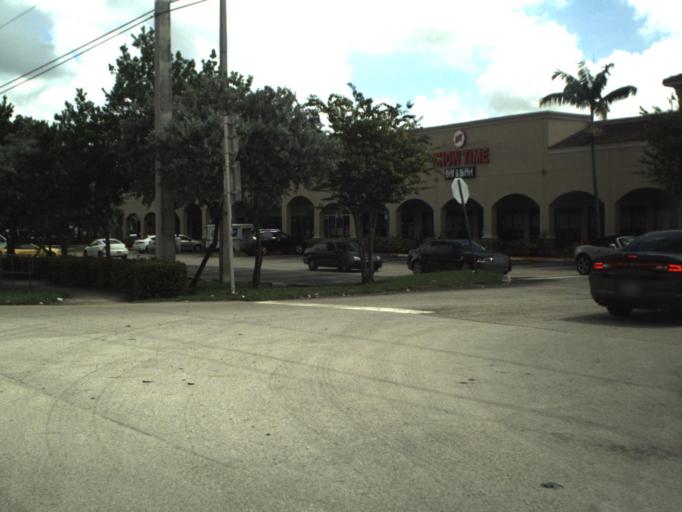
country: US
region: Florida
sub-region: Miami-Dade County
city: Country Club
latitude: 25.9948
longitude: -80.3114
